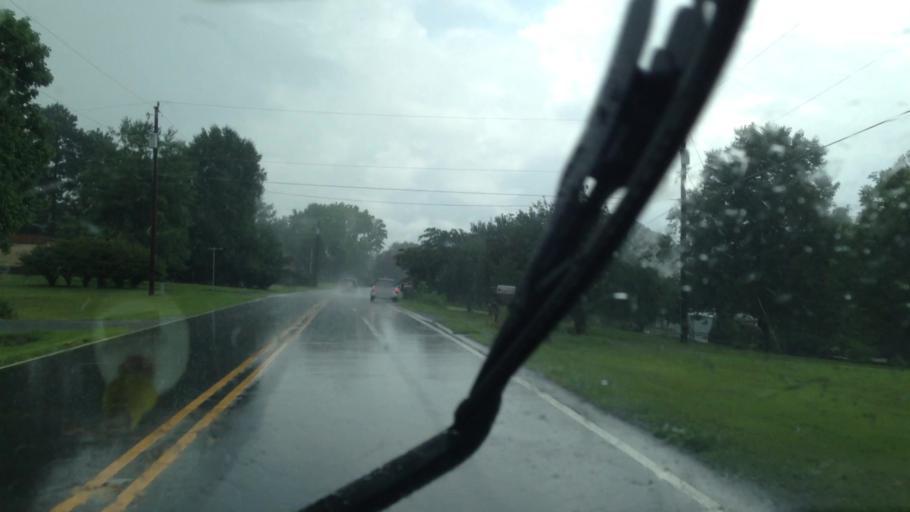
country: US
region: North Carolina
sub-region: Stokes County
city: Danbury
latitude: 36.4077
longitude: -80.0925
